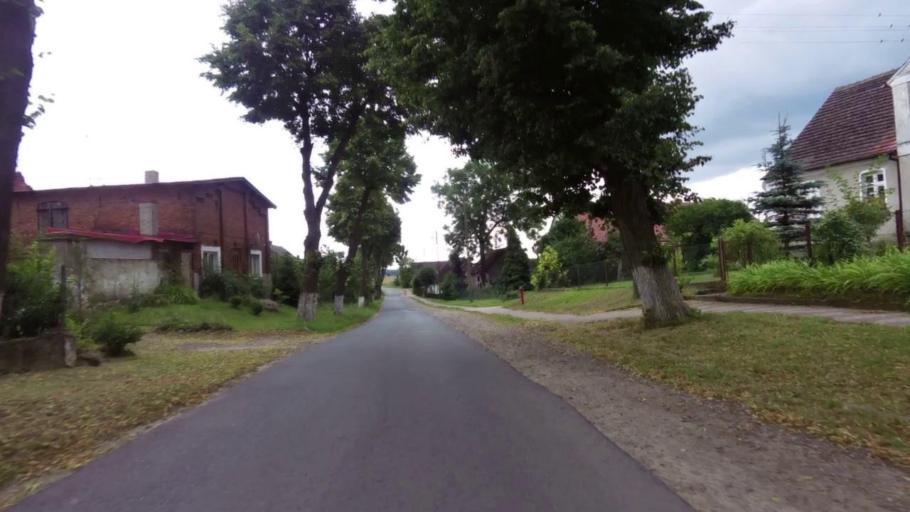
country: PL
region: West Pomeranian Voivodeship
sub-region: Powiat gryfinski
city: Chojna
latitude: 52.9084
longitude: 14.4333
